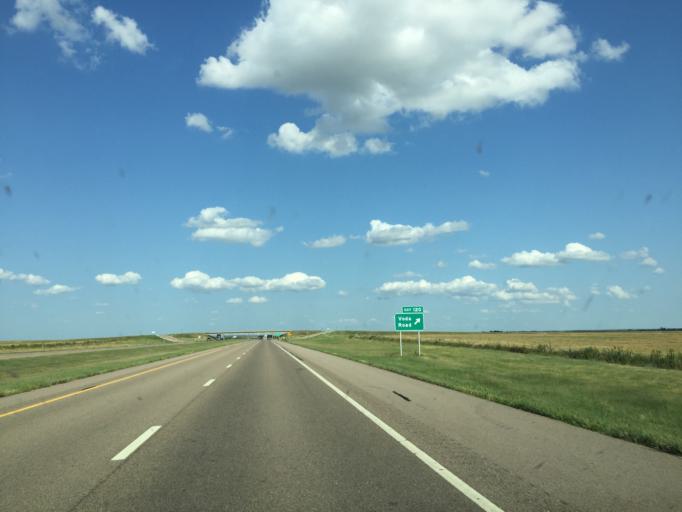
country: US
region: Kansas
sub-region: Trego County
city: WaKeeney
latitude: 39.0230
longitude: -100.0262
